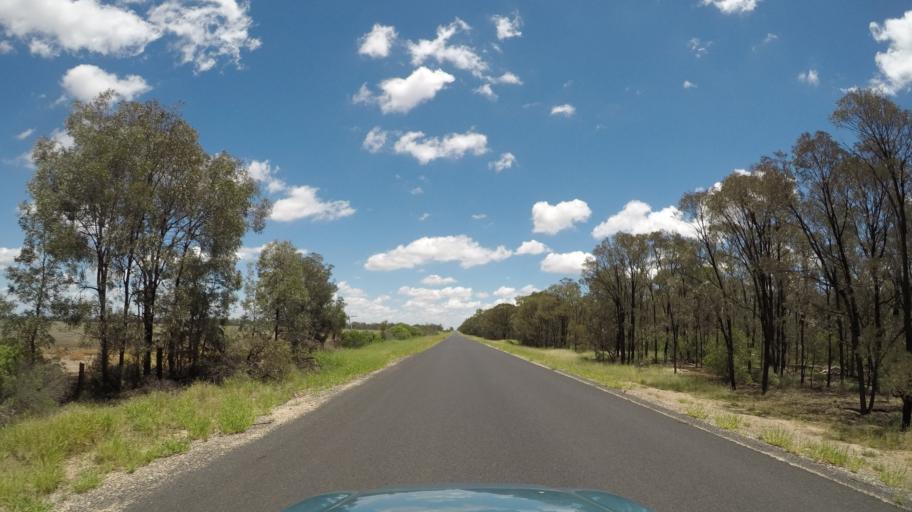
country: AU
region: Queensland
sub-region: Goondiwindi
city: Goondiwindi
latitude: -28.1628
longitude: 150.4196
